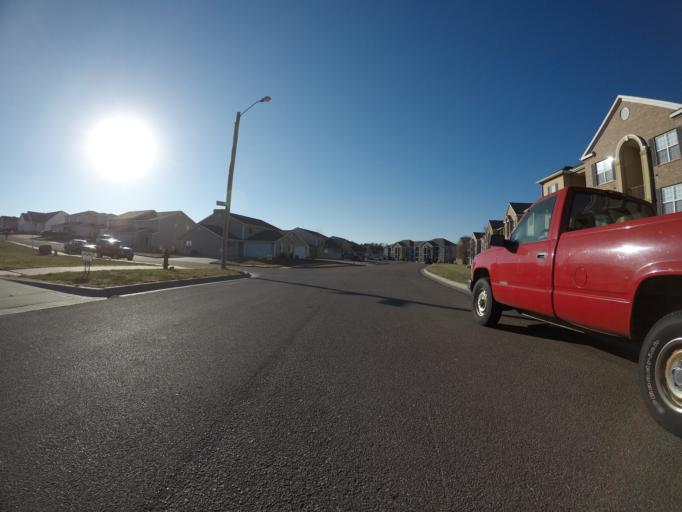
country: US
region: Kansas
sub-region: Riley County
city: Manhattan
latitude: 39.1874
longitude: -96.6466
